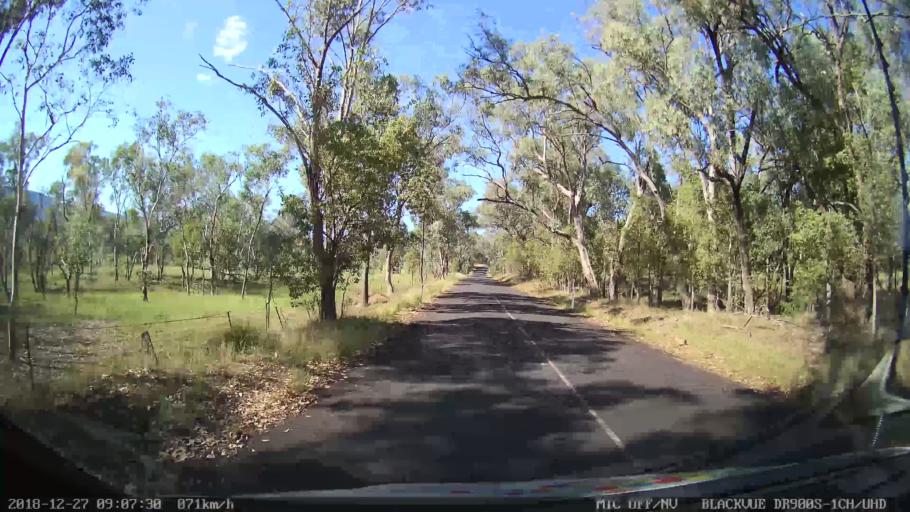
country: AU
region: New South Wales
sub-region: Lithgow
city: Portland
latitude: -33.1292
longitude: 150.1566
